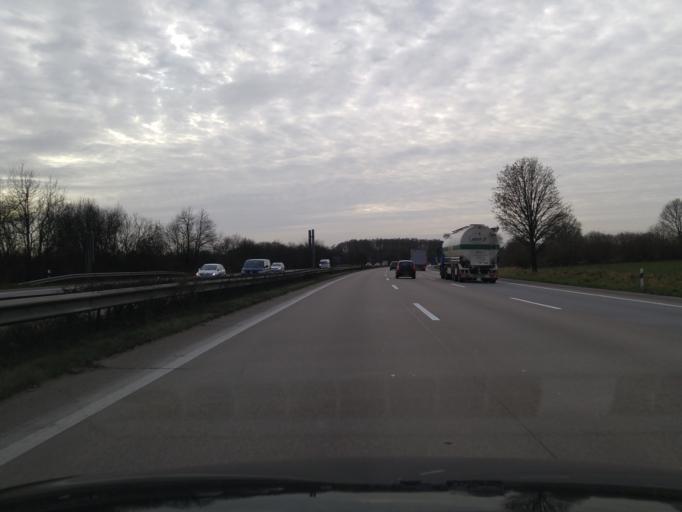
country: DE
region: Schleswig-Holstein
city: Stapelfeld
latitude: 53.6052
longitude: 10.2301
